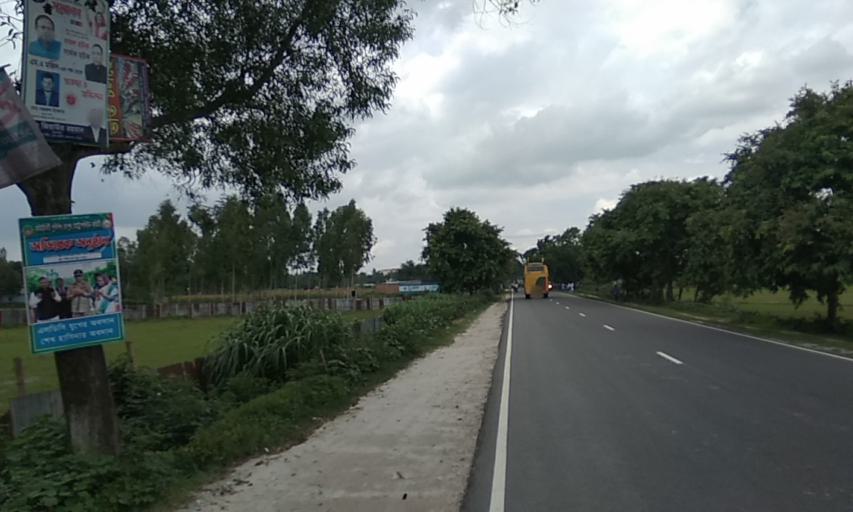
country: BD
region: Rangpur Division
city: Rangpur
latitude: 25.7969
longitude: 89.1956
